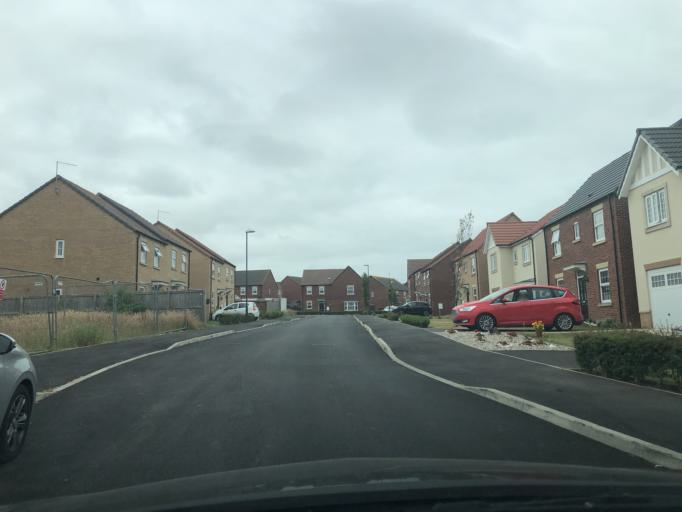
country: GB
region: England
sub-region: North Yorkshire
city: Filey
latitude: 54.2046
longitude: -0.2974
